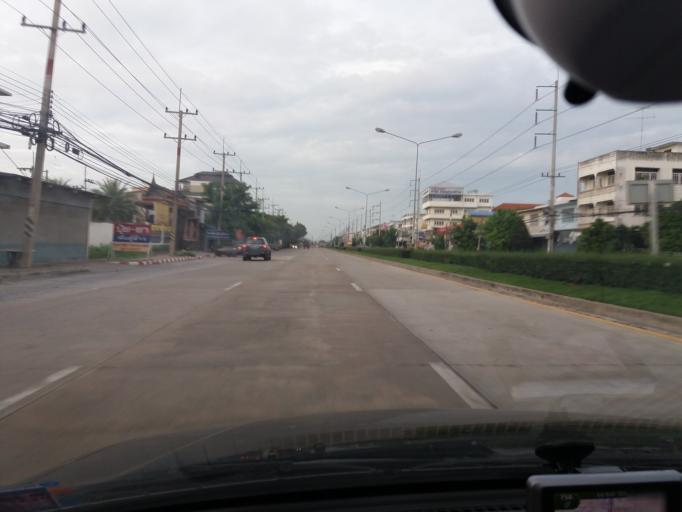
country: TH
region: Suphan Buri
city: U Thong
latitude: 14.3845
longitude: 99.8948
